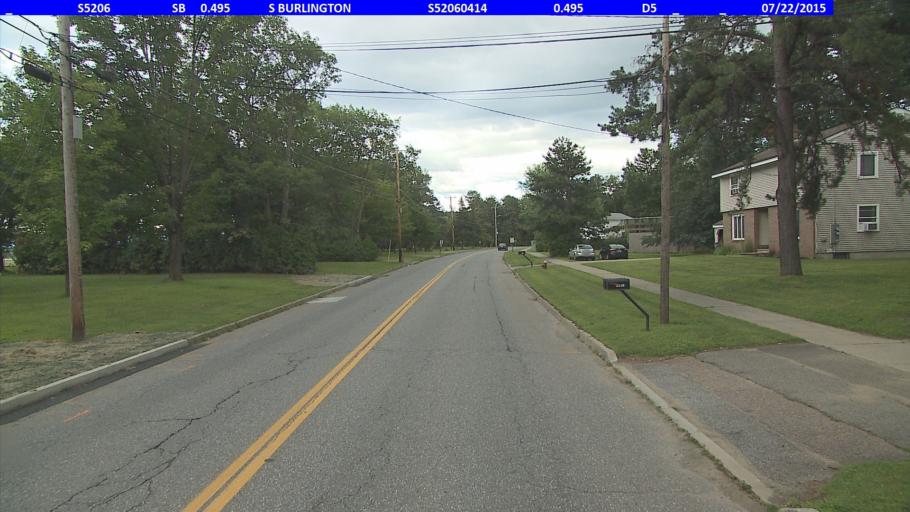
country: US
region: Vermont
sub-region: Chittenden County
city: South Burlington
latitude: 44.4772
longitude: -73.1670
